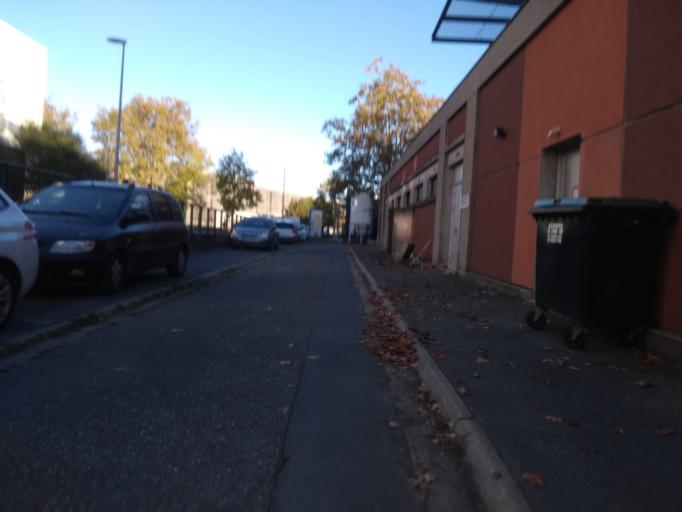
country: FR
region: Aquitaine
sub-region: Departement de la Gironde
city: Talence
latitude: 44.8020
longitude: -0.6099
